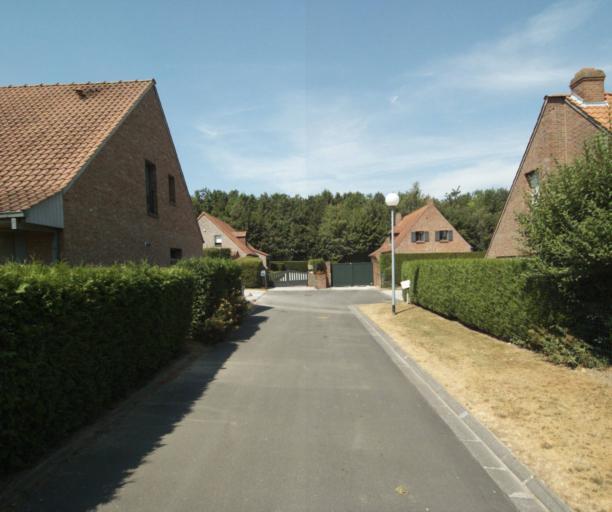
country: FR
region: Nord-Pas-de-Calais
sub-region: Departement du Nord
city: Roncq
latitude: 50.7299
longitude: 3.1164
